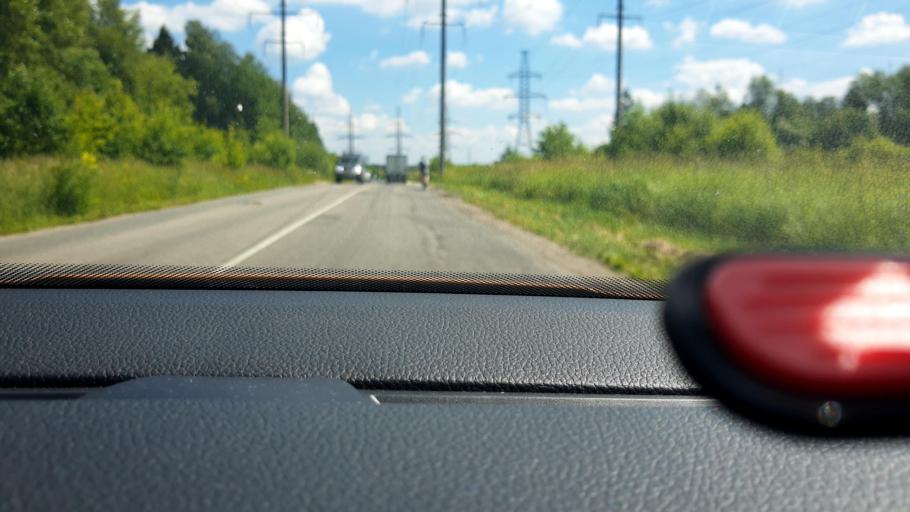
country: RU
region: Moskovskaya
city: Firsanovka
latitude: 55.9498
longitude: 37.2208
